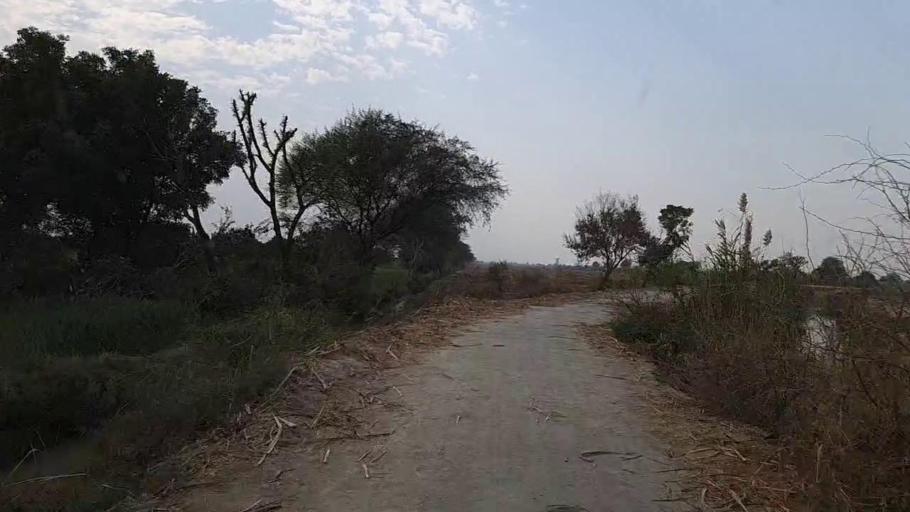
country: PK
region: Sindh
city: Mirwah Gorchani
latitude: 25.3718
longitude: 69.0730
